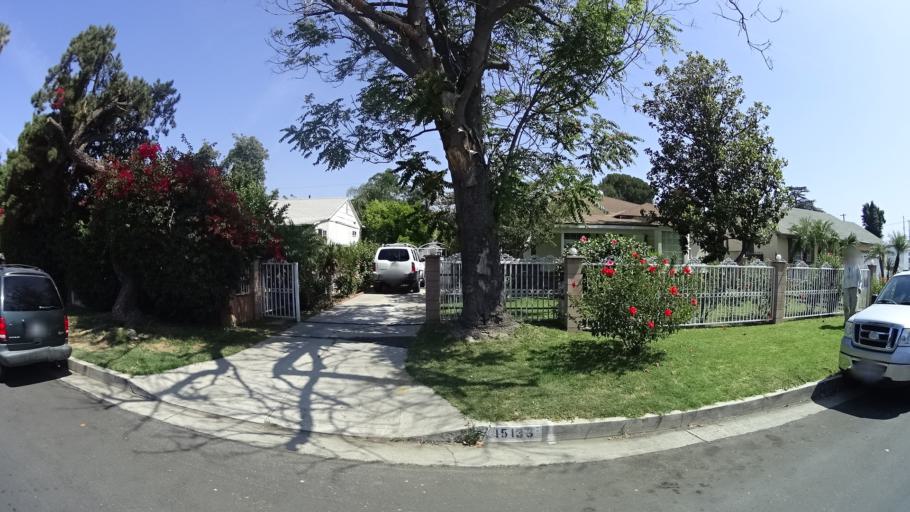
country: US
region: California
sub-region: Los Angeles County
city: Van Nuys
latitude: 34.2066
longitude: -118.4630
